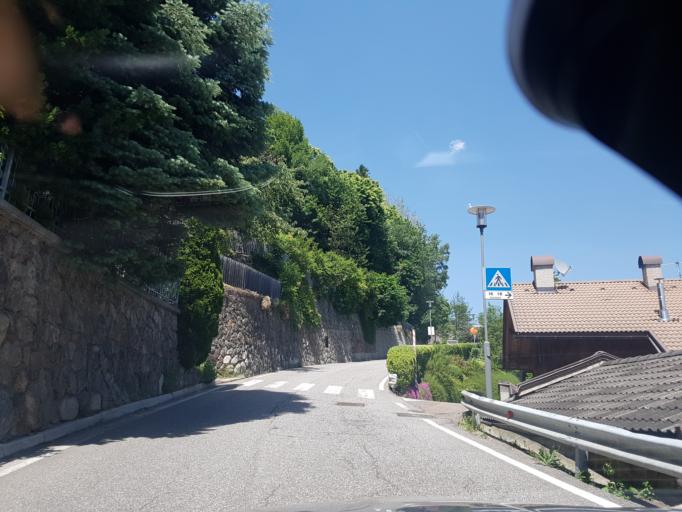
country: IT
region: Trentino-Alto Adige
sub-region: Bolzano
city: Villandro - Villanders
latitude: 46.6308
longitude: 11.5367
